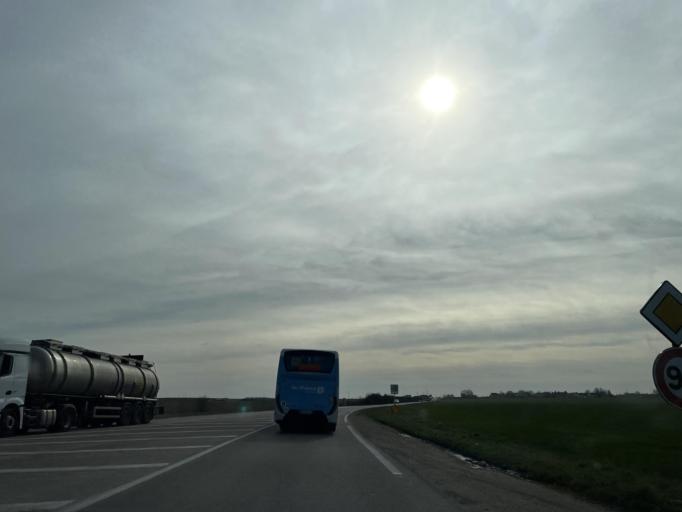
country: FR
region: Ile-de-France
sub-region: Departement de Seine-et-Marne
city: Jouy-le-Chatel
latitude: 48.6822
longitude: 3.1068
